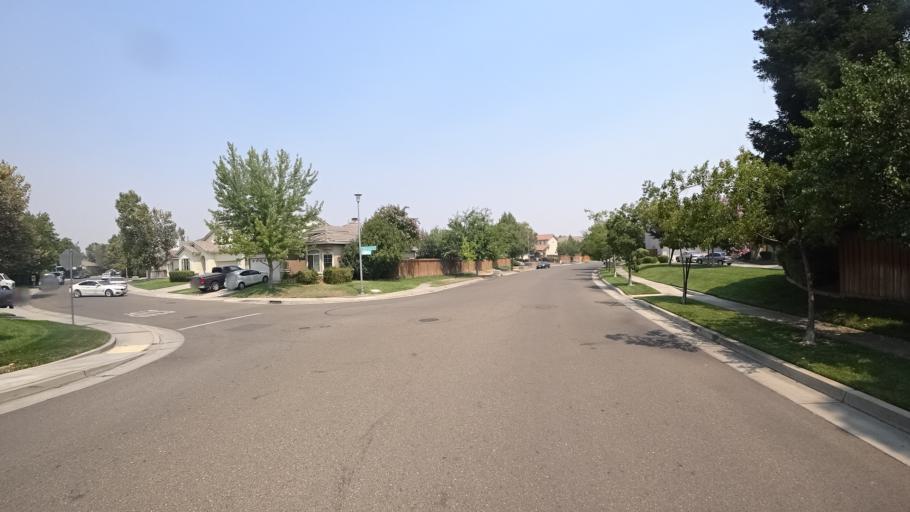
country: US
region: California
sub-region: Sacramento County
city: Laguna
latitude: 38.4061
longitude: -121.4340
